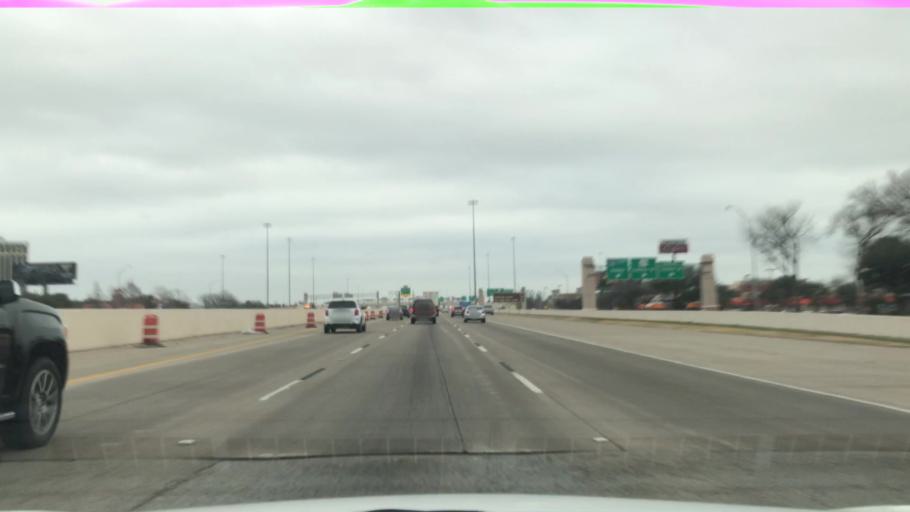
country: US
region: Texas
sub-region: Tarrant County
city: Arlington
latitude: 32.7597
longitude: -97.1102
